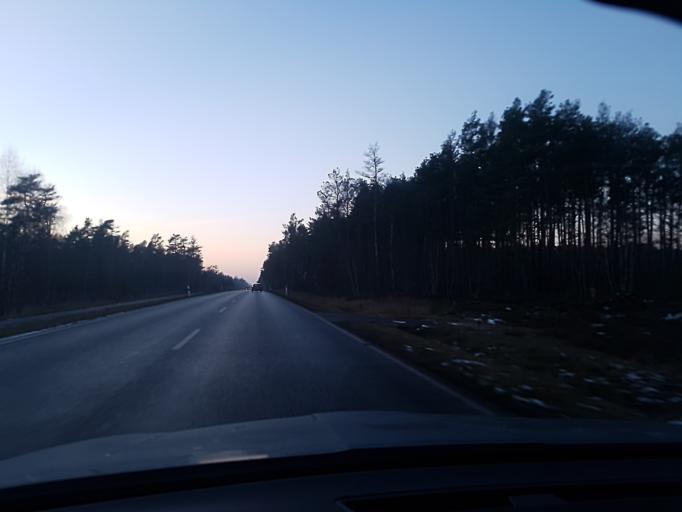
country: DE
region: Brandenburg
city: Finsterwalde
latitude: 51.6328
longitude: 13.6658
